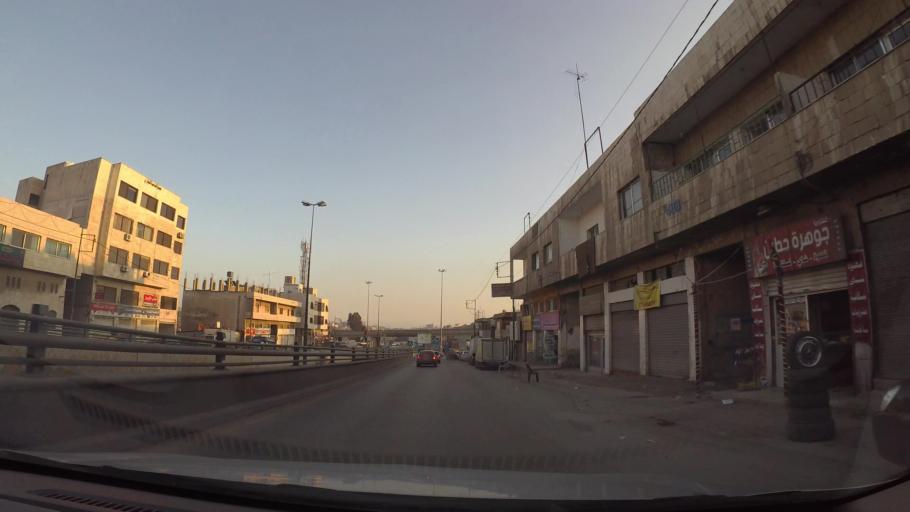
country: JO
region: Amman
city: Al Quwaysimah
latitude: 31.9022
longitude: 35.9374
